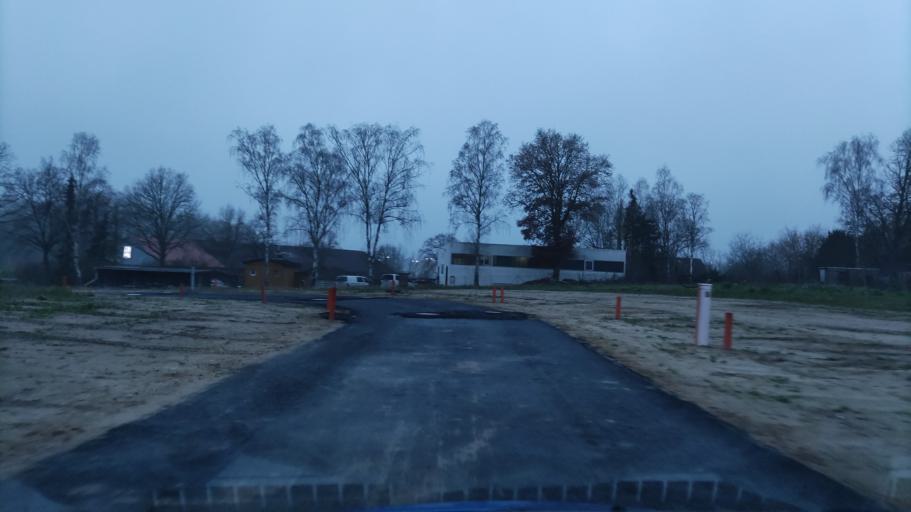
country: DE
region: Lower Saxony
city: Dahlem
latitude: 53.1838
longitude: 10.7553
